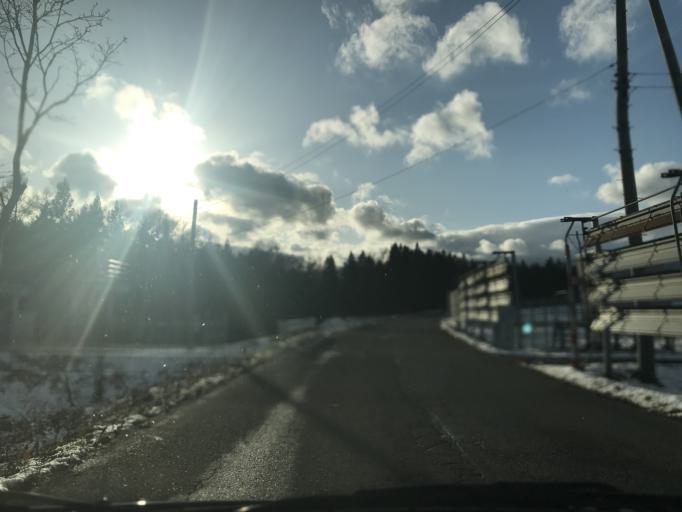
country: JP
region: Iwate
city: Kitakami
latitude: 39.2446
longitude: 141.0010
